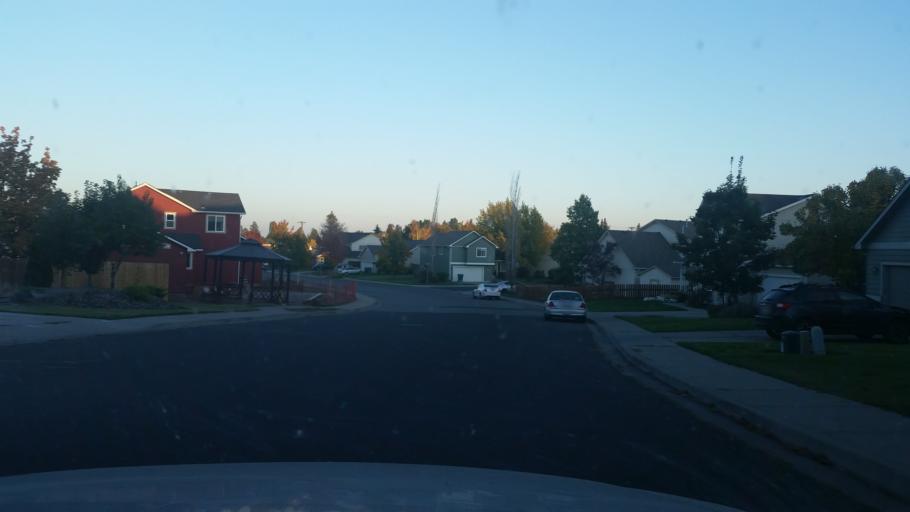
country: US
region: Washington
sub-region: Spokane County
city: Cheney
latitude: 47.5014
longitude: -117.5779
